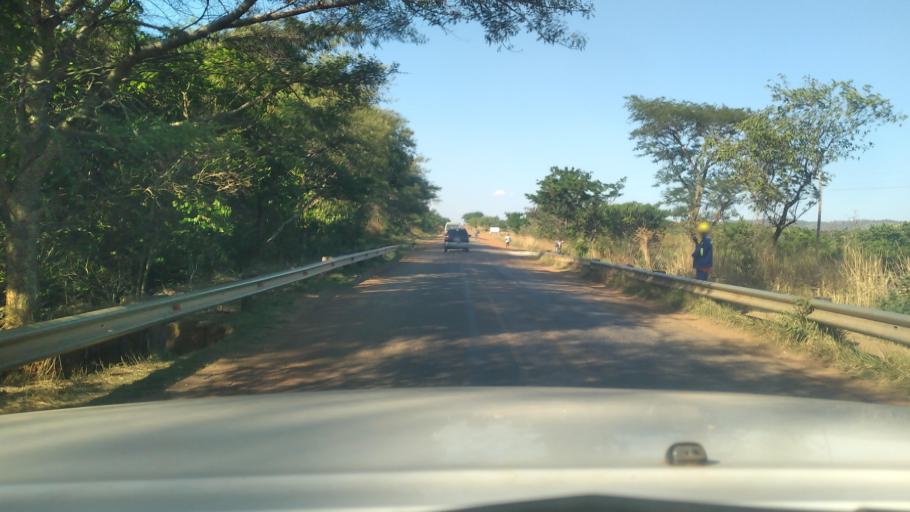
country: ZM
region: Northern
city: Mpika
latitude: -11.7421
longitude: 31.4686
